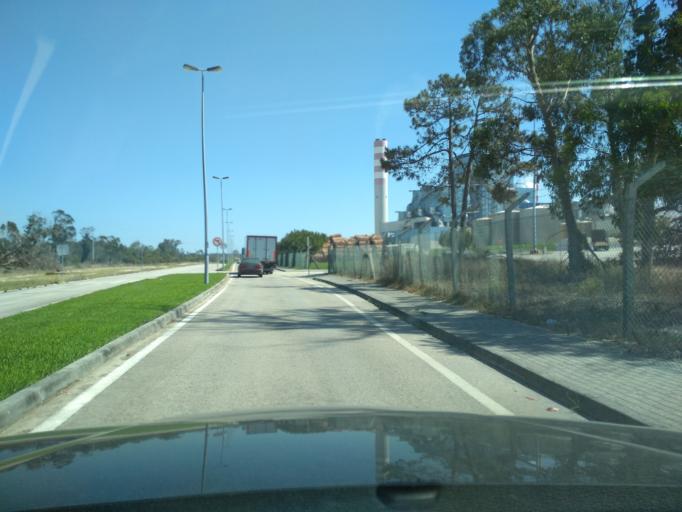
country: PT
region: Coimbra
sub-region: Figueira da Foz
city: Lavos
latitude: 40.0555
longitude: -8.8802
